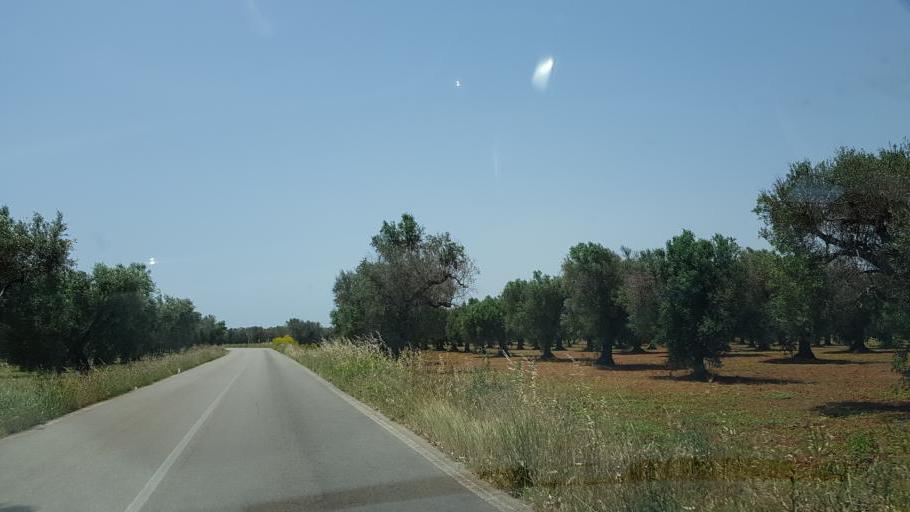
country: IT
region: Apulia
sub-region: Provincia di Lecce
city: Veglie
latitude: 40.3232
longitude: 17.9088
